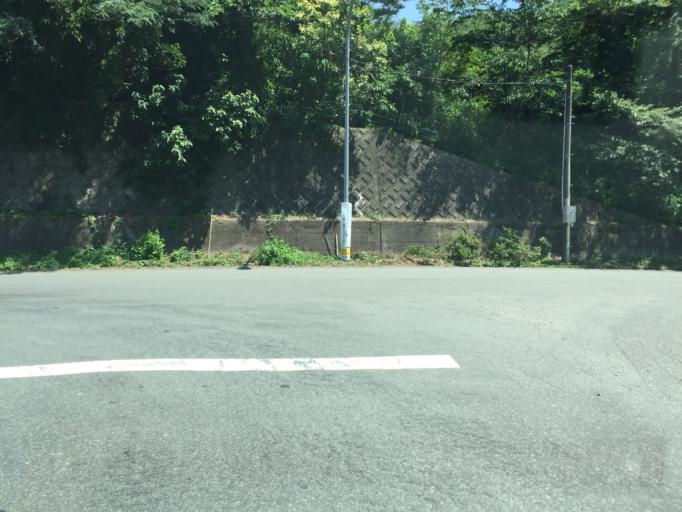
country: JP
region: Fukushima
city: Yanagawamachi-saiwaicho
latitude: 37.8926
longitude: 140.6447
